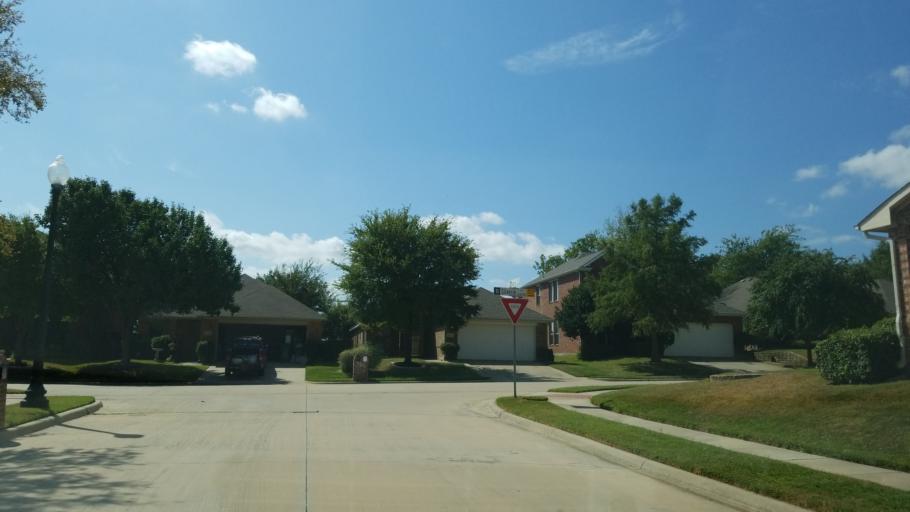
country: US
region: Texas
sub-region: Tarrant County
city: Euless
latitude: 32.8561
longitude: -97.1056
